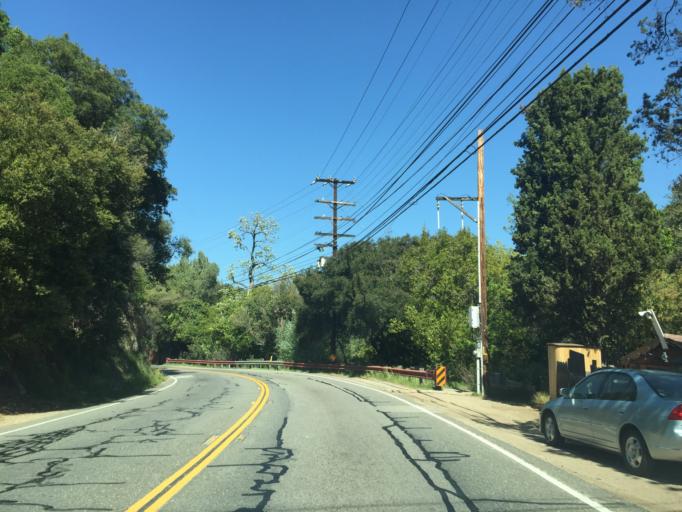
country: US
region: California
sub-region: Los Angeles County
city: Topanga
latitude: 34.0878
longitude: -118.6010
